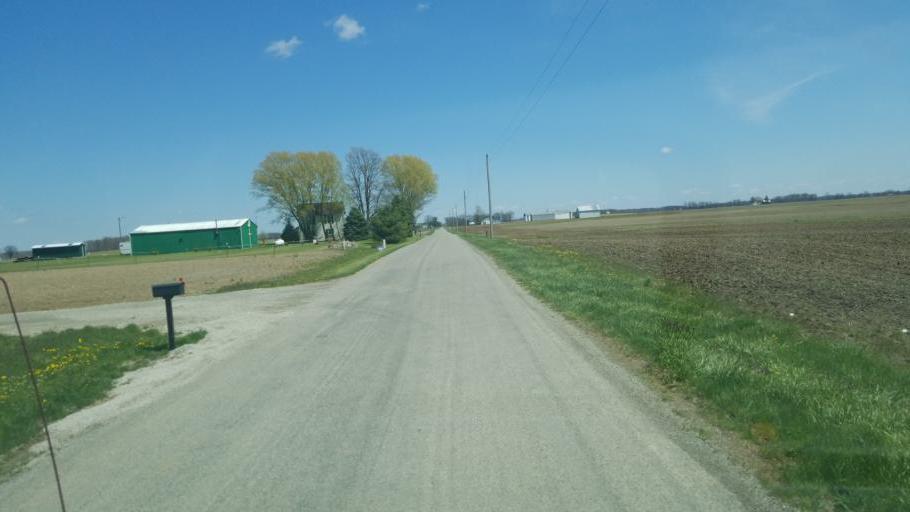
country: US
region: Ohio
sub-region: Union County
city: Richwood
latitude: 40.4920
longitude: -83.2769
